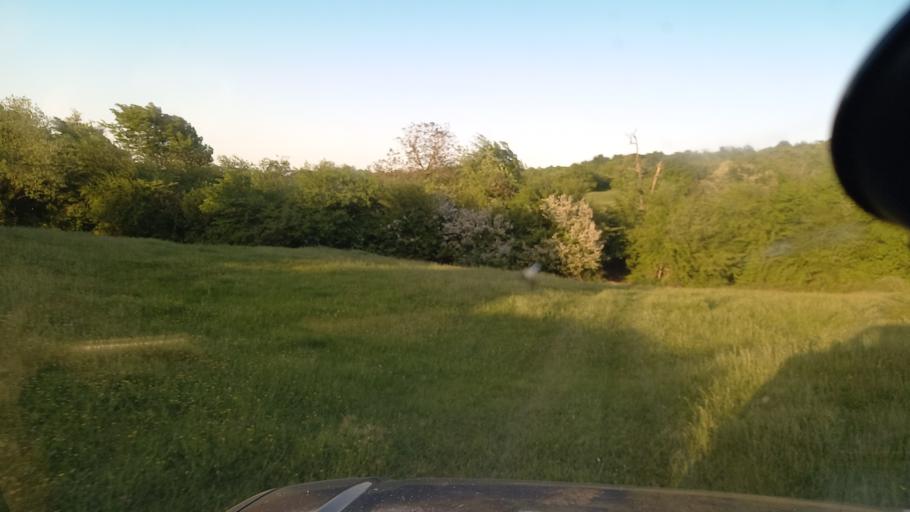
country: RU
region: Dagestan
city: Khuchni
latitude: 42.0080
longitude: 47.9735
